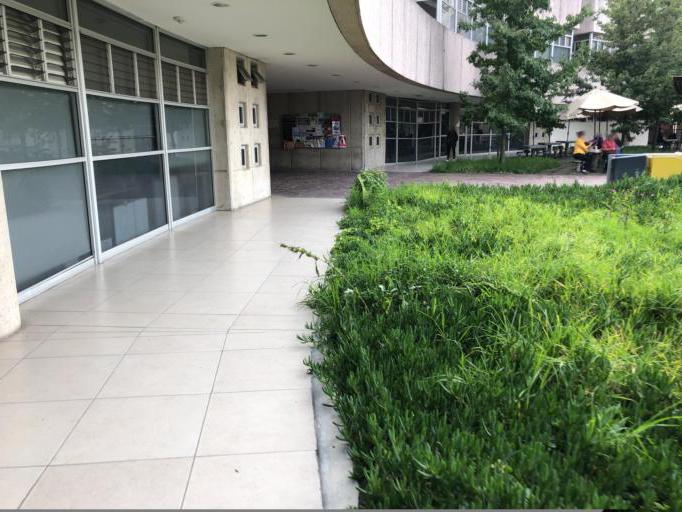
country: MX
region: Mexico City
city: Tlalpan
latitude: 19.3096
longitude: -99.1852
